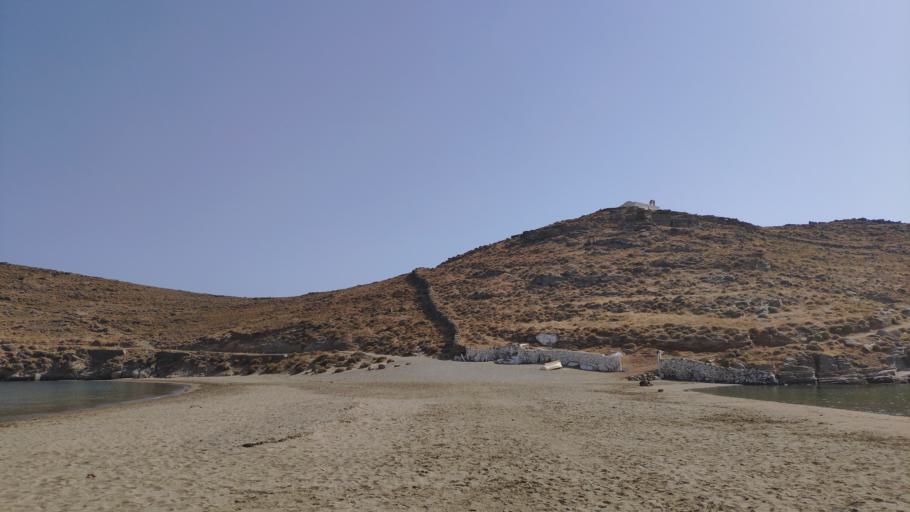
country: GR
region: South Aegean
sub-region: Nomos Kykladon
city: Kythnos
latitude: 37.4141
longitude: 24.3788
